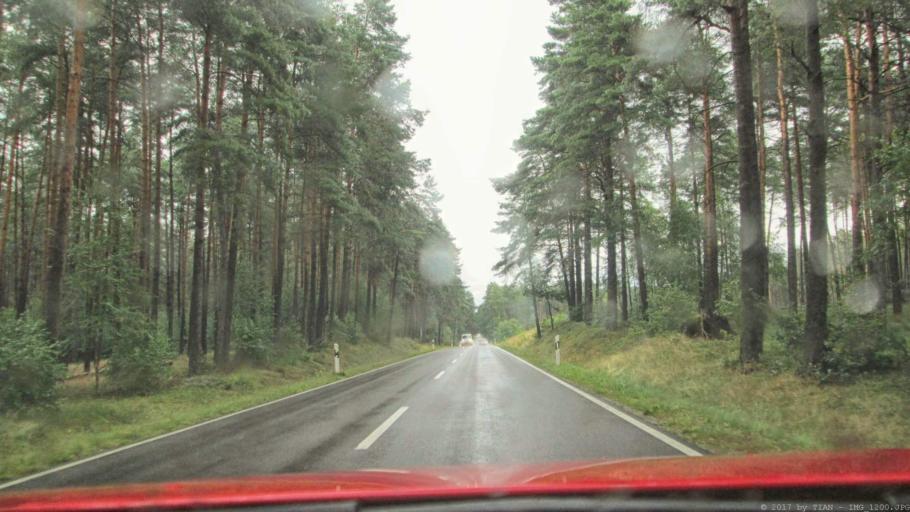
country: DE
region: Lower Saxony
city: Bergfeld
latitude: 52.6092
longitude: 10.8068
